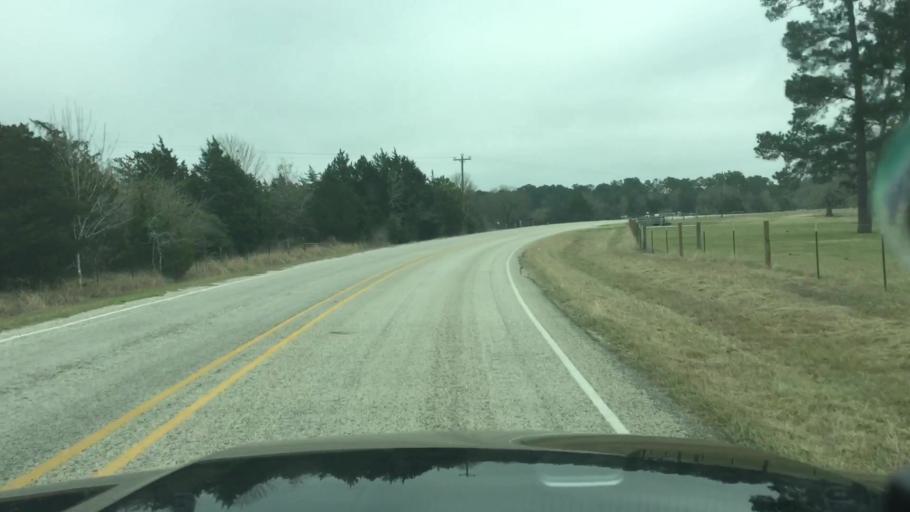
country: US
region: Texas
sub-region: Fayette County
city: La Grange
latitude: 30.0130
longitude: -96.9323
